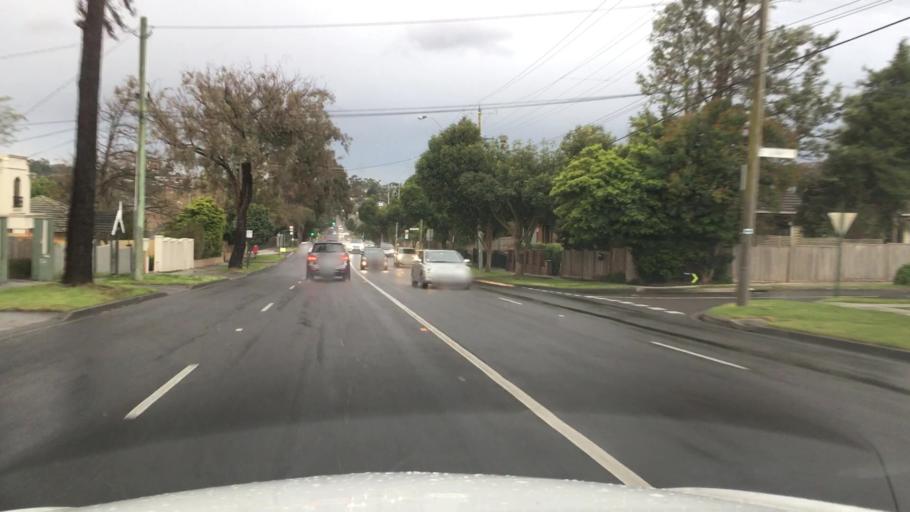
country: AU
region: Victoria
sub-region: Whitehorse
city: Burwood
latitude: -37.8467
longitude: 145.1206
